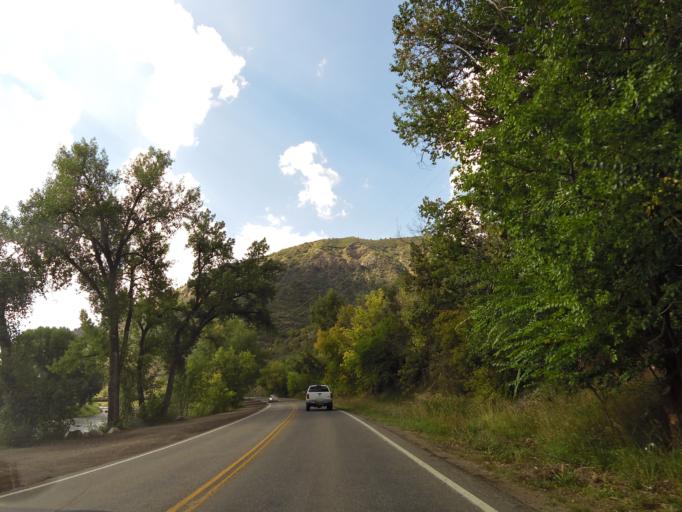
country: US
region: Colorado
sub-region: La Plata County
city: Durango
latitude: 37.2718
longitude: -107.8868
